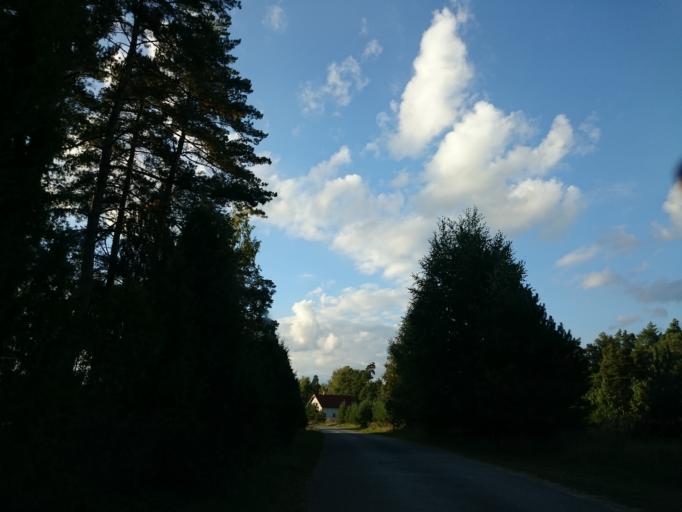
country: LV
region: Adazi
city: Adazi
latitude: 57.0652
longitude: 24.2747
